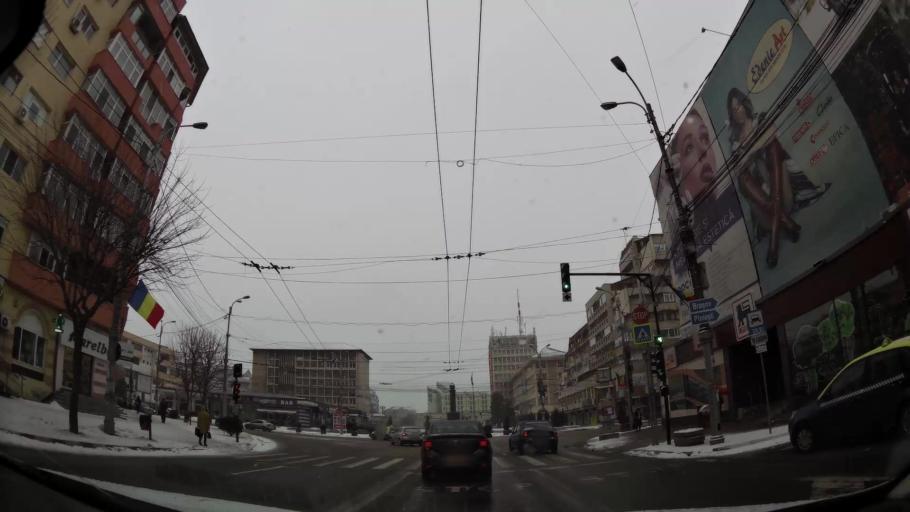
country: RO
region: Dambovita
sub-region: Municipiul Targoviste
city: Targoviste
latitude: 44.9261
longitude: 25.4634
